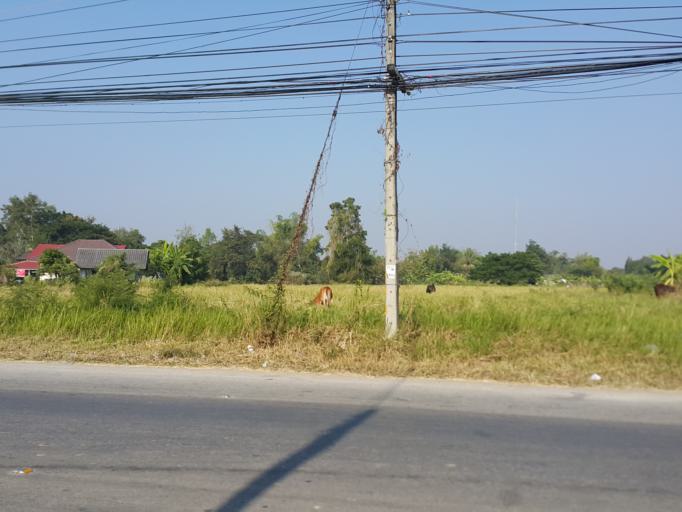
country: TH
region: Chiang Mai
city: San Kamphaeng
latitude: 18.7849
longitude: 99.0956
